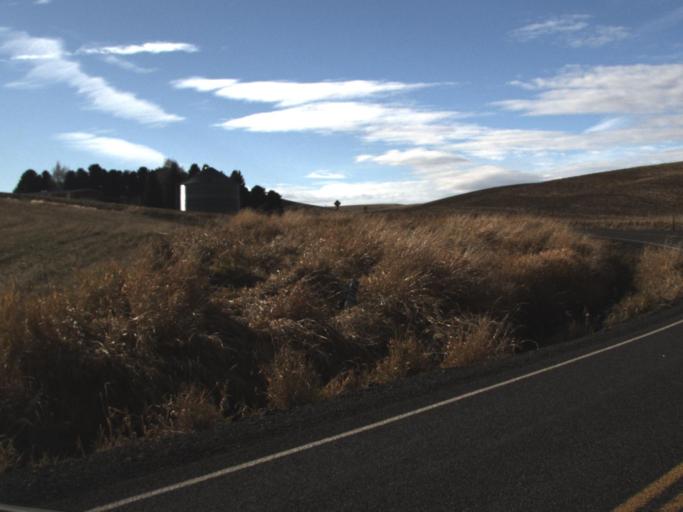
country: US
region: Washington
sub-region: Whitman County
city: Pullman
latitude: 46.9417
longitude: -117.1591
